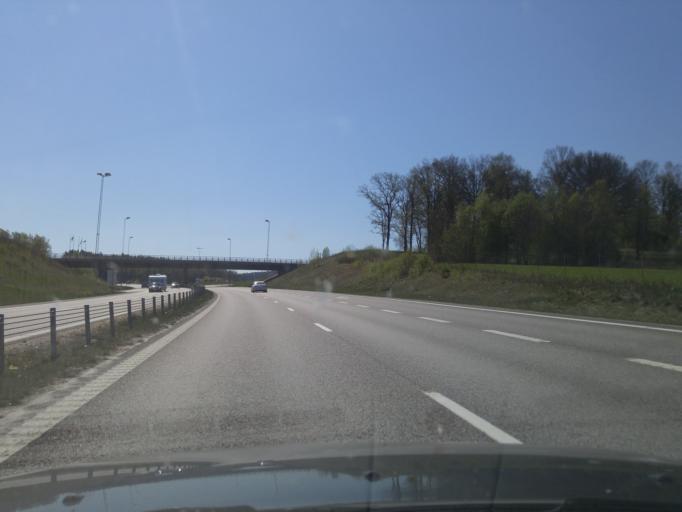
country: SE
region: Vaestra Goetaland
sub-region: Munkedals Kommun
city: Munkedal
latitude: 58.4616
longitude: 11.6552
